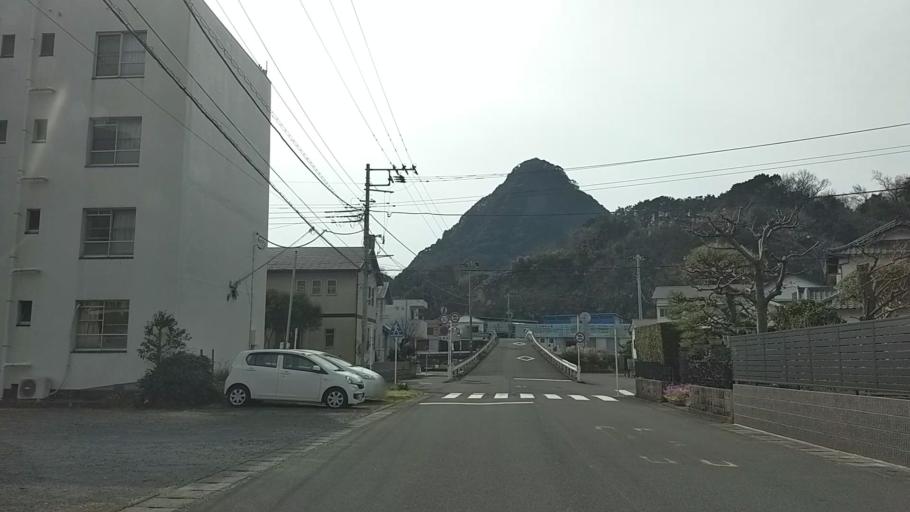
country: JP
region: Shizuoka
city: Shimoda
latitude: 34.6883
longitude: 138.9417
